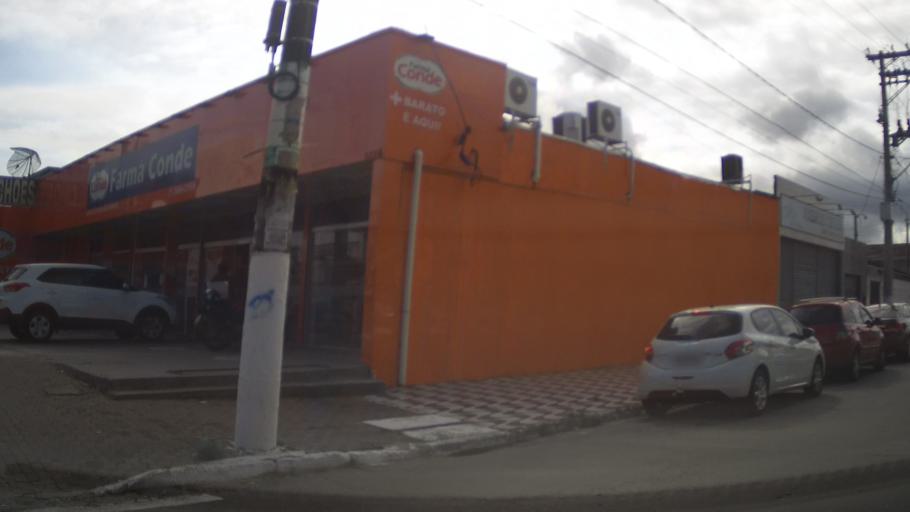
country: BR
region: Sao Paulo
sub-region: Praia Grande
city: Praia Grande
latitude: -24.0184
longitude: -46.4593
